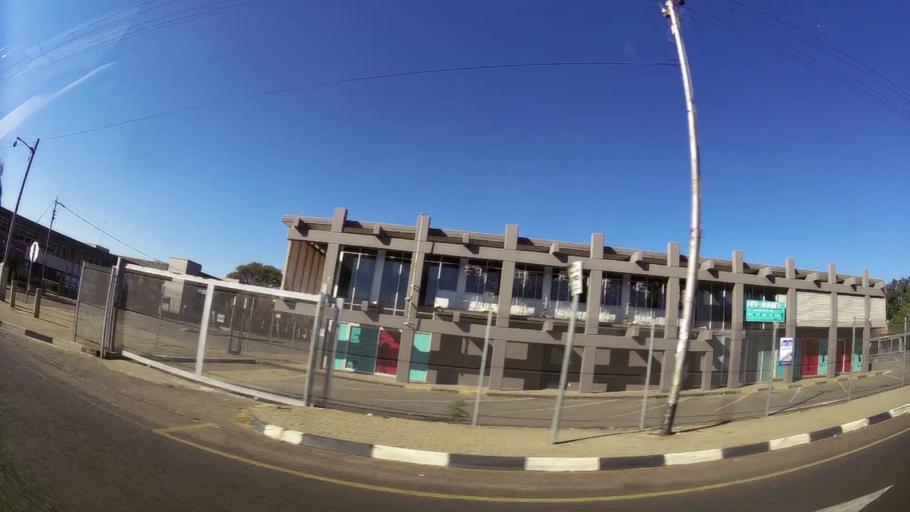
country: ZA
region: Gauteng
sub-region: City of Tshwane Metropolitan Municipality
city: Centurion
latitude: -25.8302
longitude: 28.2042
